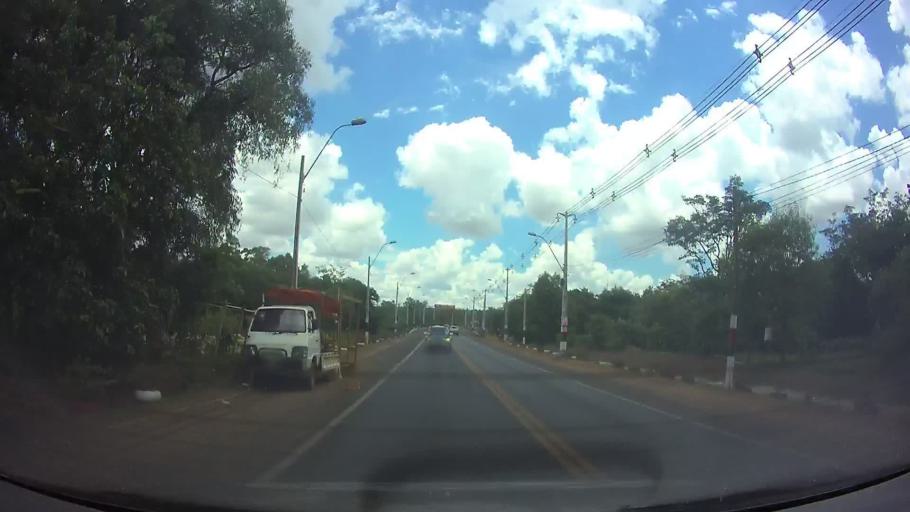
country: PY
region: Central
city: Aregua
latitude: -25.2929
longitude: -57.4433
